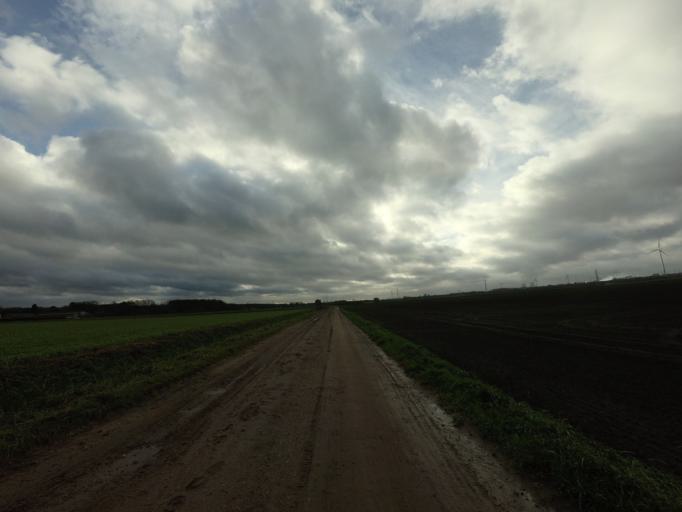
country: NL
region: North Brabant
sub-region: Gemeente Woensdrecht
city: Woensdrecht
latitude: 51.3799
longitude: 4.3291
